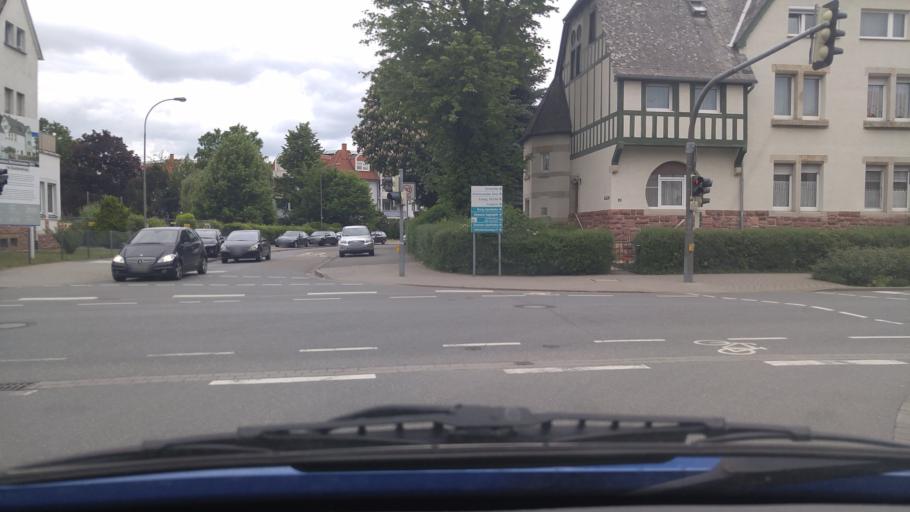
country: DE
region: Hesse
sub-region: Regierungsbezirk Darmstadt
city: Ginsheim-Gustavsburg
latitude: 49.9969
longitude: 8.3191
